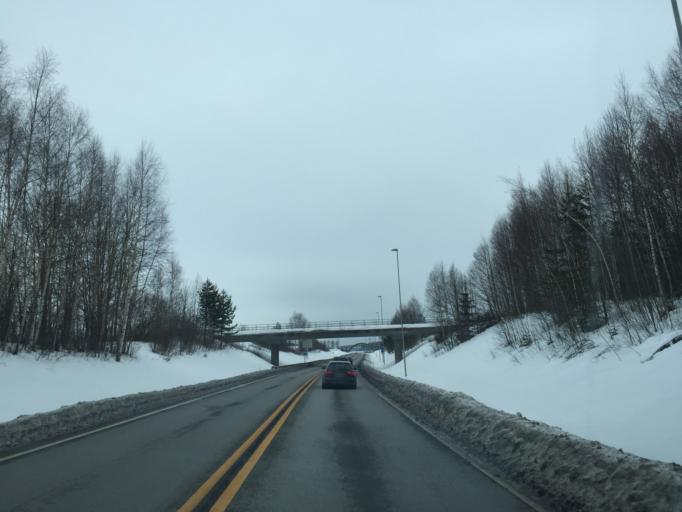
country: NO
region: Hedmark
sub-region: Loten
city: Loten
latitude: 60.7952
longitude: 11.2938
